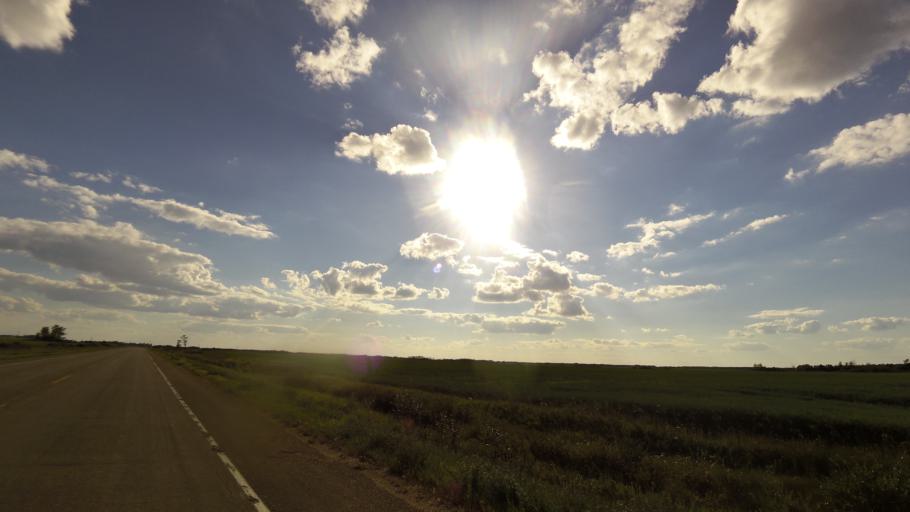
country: CA
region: Saskatchewan
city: Lanigan
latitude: 51.8713
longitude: -105.1993
